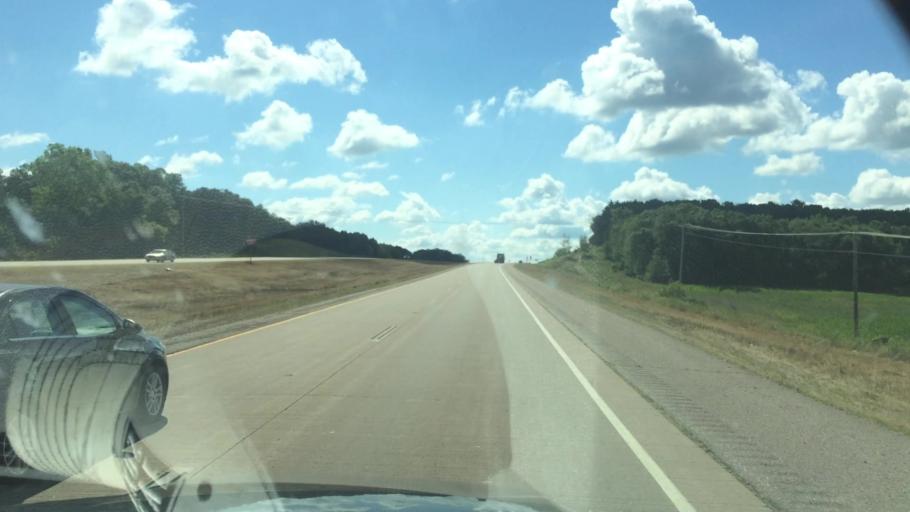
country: US
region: Wisconsin
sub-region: Portage County
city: Amherst
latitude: 44.4186
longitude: -89.2507
